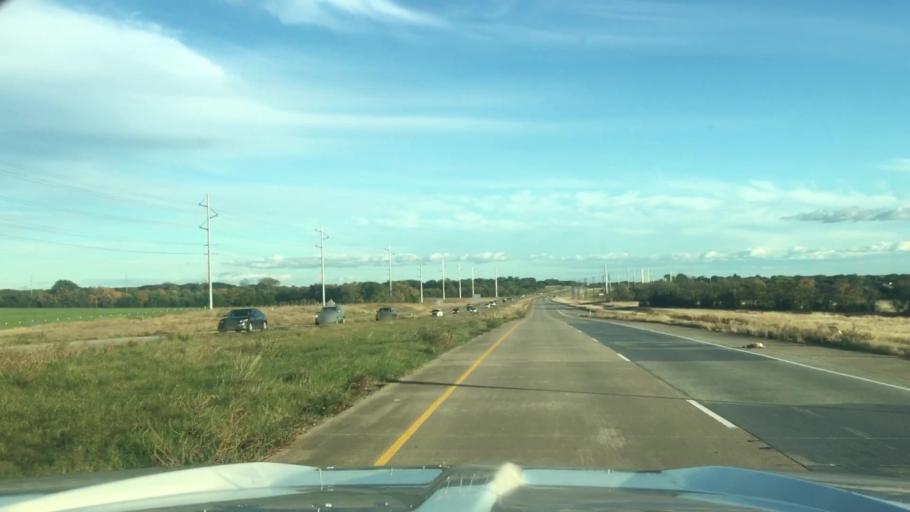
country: US
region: Texas
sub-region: Denton County
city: Denton
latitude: 33.2572
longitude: -97.1084
